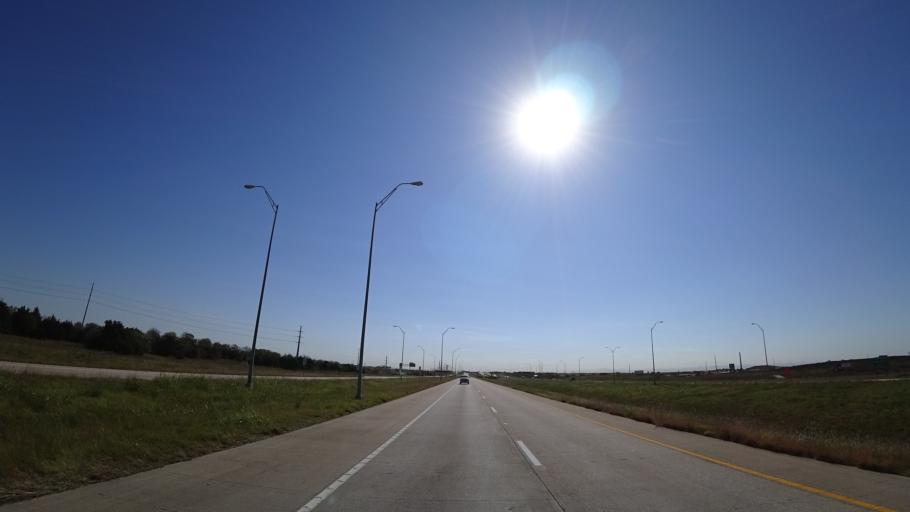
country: US
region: Texas
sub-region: Travis County
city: Pflugerville
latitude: 30.4193
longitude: -97.5865
